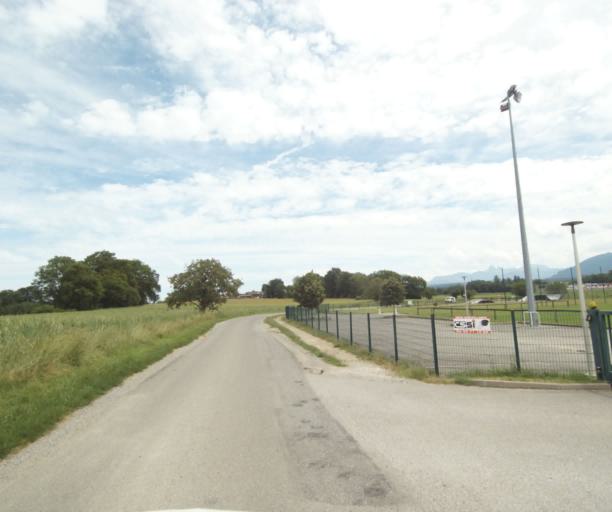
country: FR
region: Rhone-Alpes
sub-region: Departement de la Haute-Savoie
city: Anthy-sur-Leman
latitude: 46.3483
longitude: 6.4183
